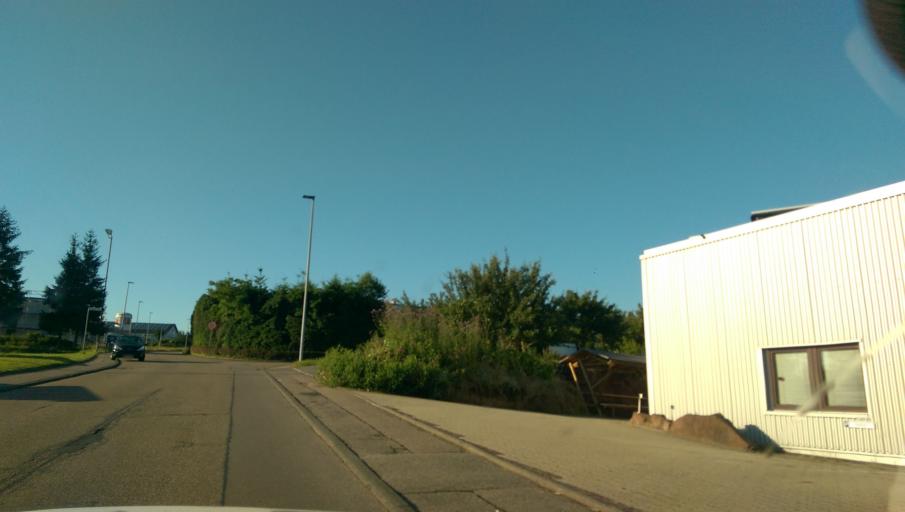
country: DE
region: Baden-Wuerttemberg
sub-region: Karlsruhe Region
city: Dobel
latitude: 48.8485
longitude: 8.5218
